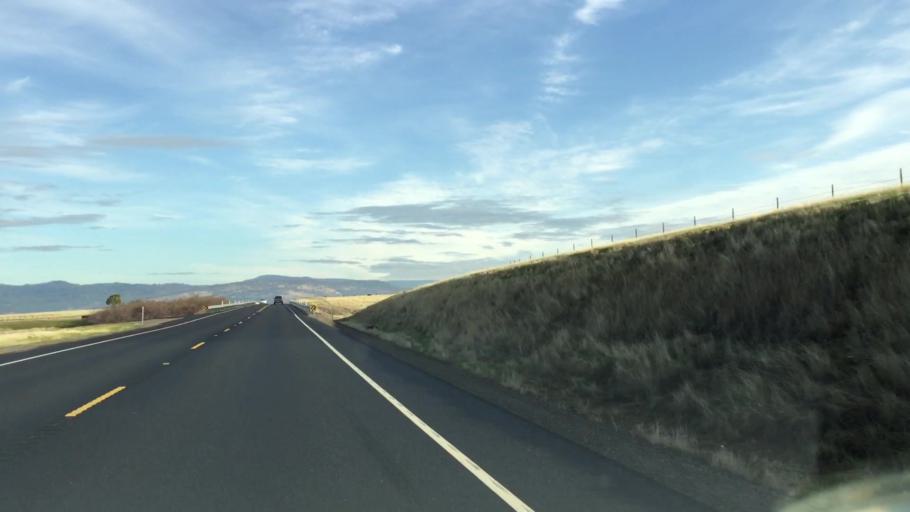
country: US
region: California
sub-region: Butte County
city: Thermalito
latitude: 39.6148
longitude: -121.6047
